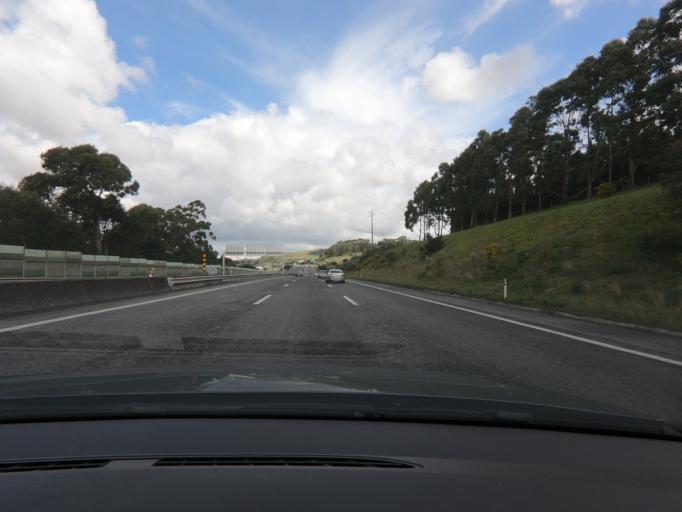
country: PT
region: Lisbon
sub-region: Oeiras
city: Quejas
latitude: 38.7235
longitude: -9.2734
